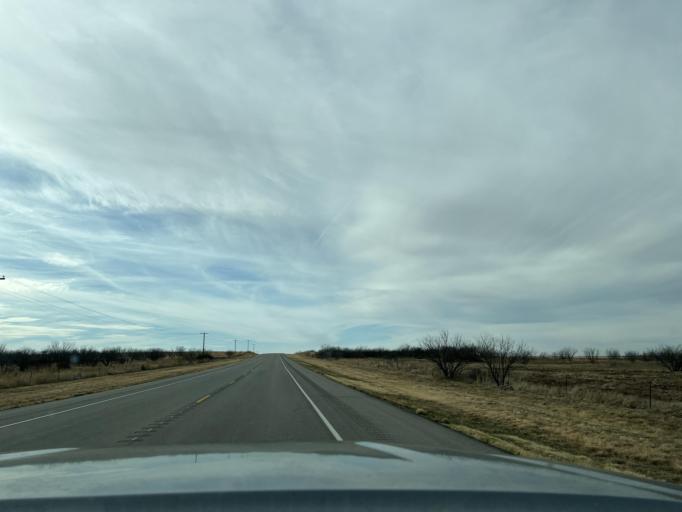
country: US
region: Texas
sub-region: Jones County
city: Anson
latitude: 32.7505
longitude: -99.6752
